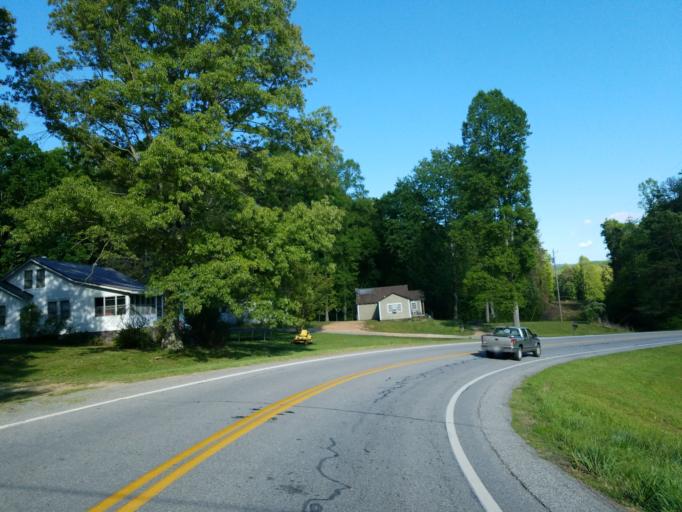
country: US
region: Georgia
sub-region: Fannin County
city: Blue Ridge
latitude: 34.8676
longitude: -84.2331
